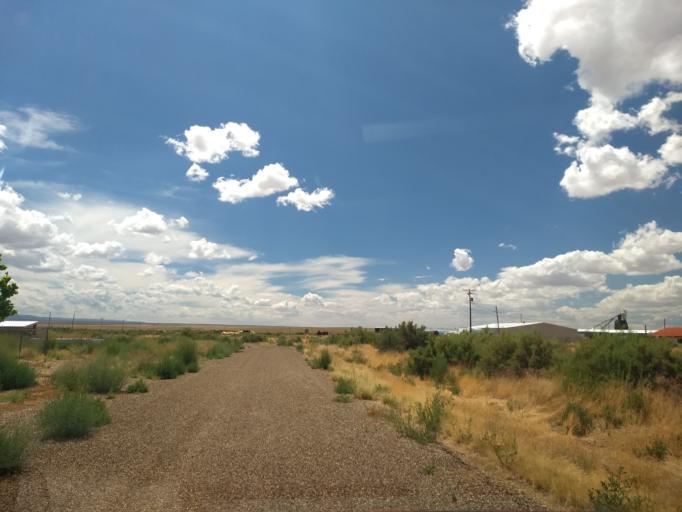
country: US
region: Arizona
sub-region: Coconino County
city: Fredonia
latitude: 36.9410
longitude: -112.5193
